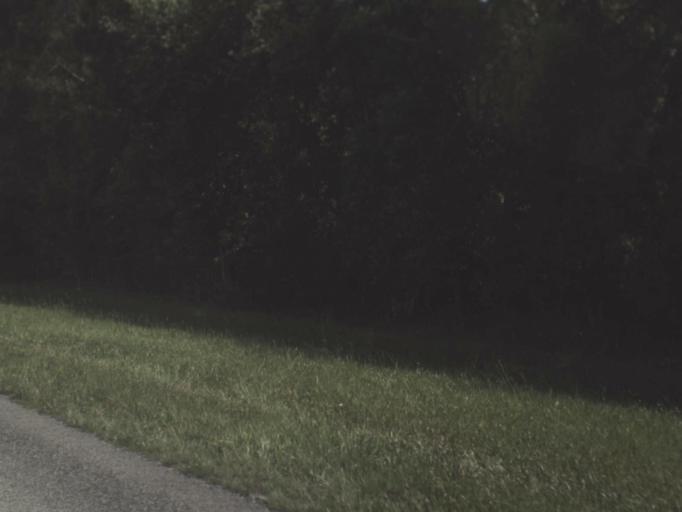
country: US
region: Florida
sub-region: Alachua County
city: Waldo
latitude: 29.7100
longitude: -82.1372
